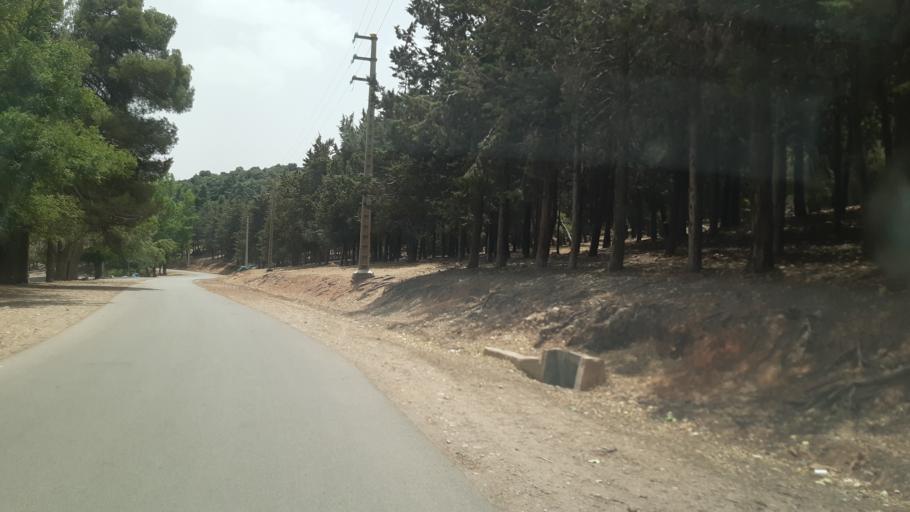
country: MA
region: Meknes-Tafilalet
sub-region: Ifrane
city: Ifrane
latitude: 33.6548
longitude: -5.0449
